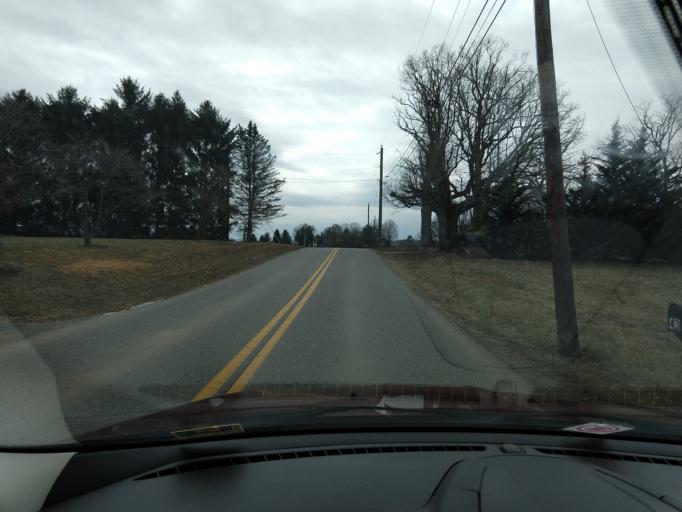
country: US
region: Virginia
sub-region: Augusta County
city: Crimora
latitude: 38.1746
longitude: -78.9154
